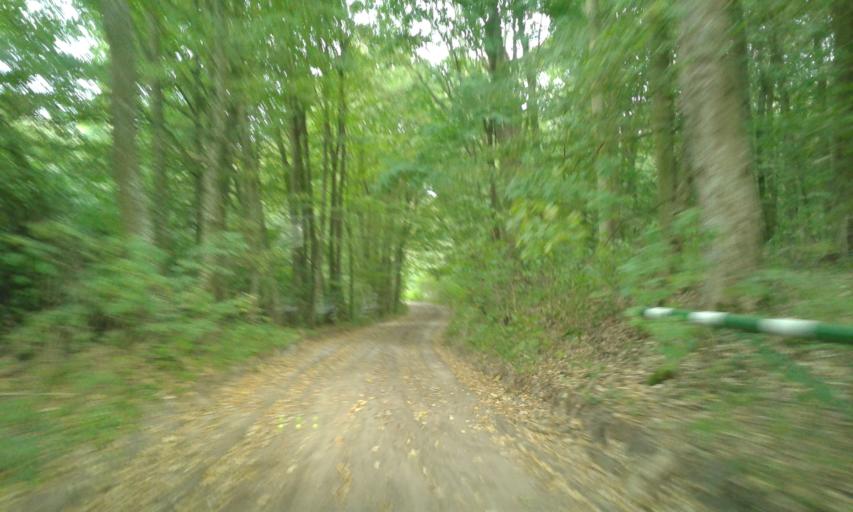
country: PL
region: West Pomeranian Voivodeship
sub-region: Powiat stargardzki
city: Dolice
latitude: 53.1801
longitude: 15.2354
